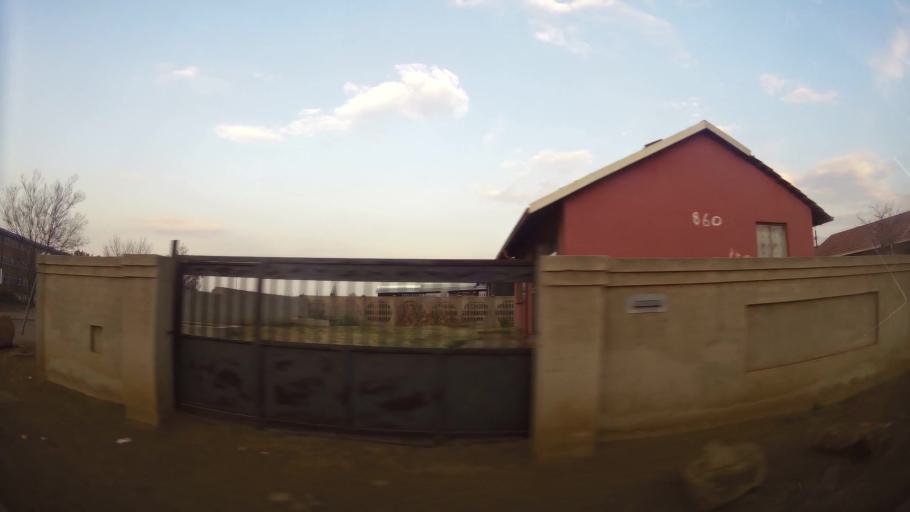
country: ZA
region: Gauteng
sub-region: City of Johannesburg Metropolitan Municipality
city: Orange Farm
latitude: -26.5465
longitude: 27.8815
